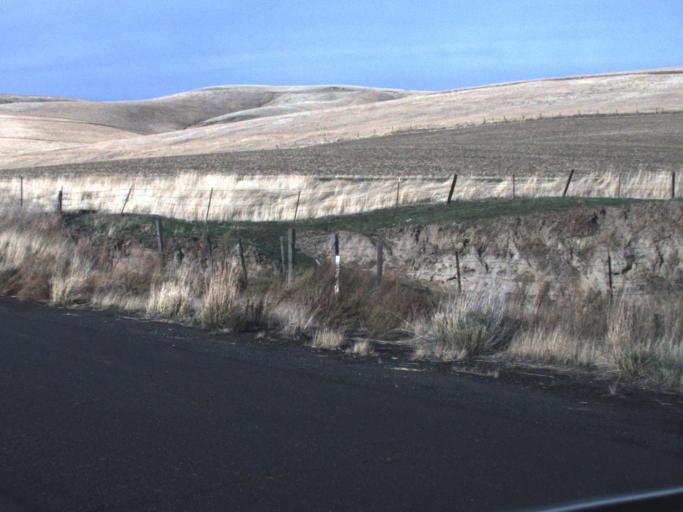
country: US
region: Washington
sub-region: Garfield County
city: Pomeroy
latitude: 46.4807
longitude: -117.7357
